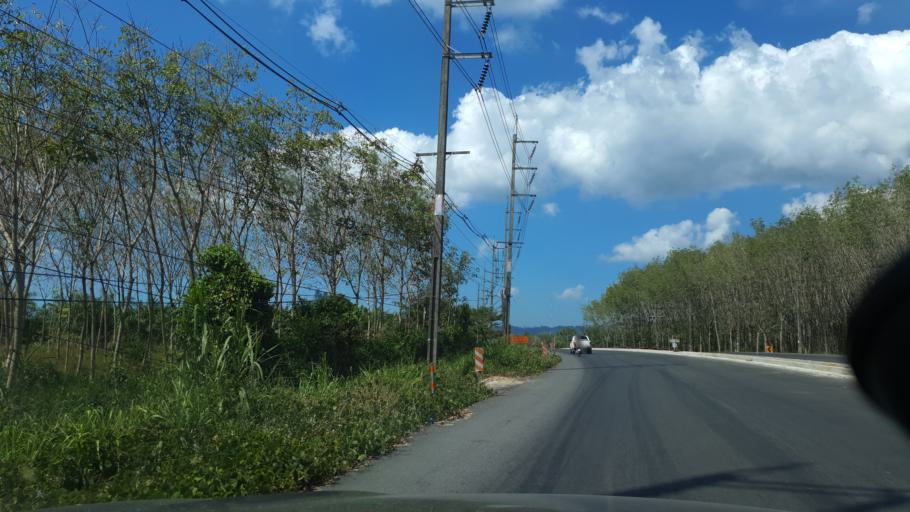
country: TH
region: Phangnga
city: Ban Khao Lak
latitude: 8.5554
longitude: 98.2707
